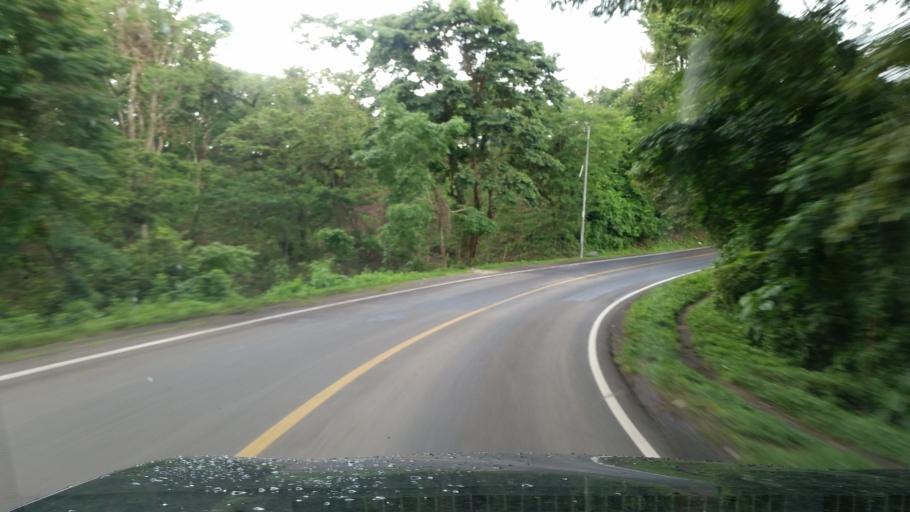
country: NI
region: Matagalpa
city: San Ramon
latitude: 13.0556
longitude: -85.7540
